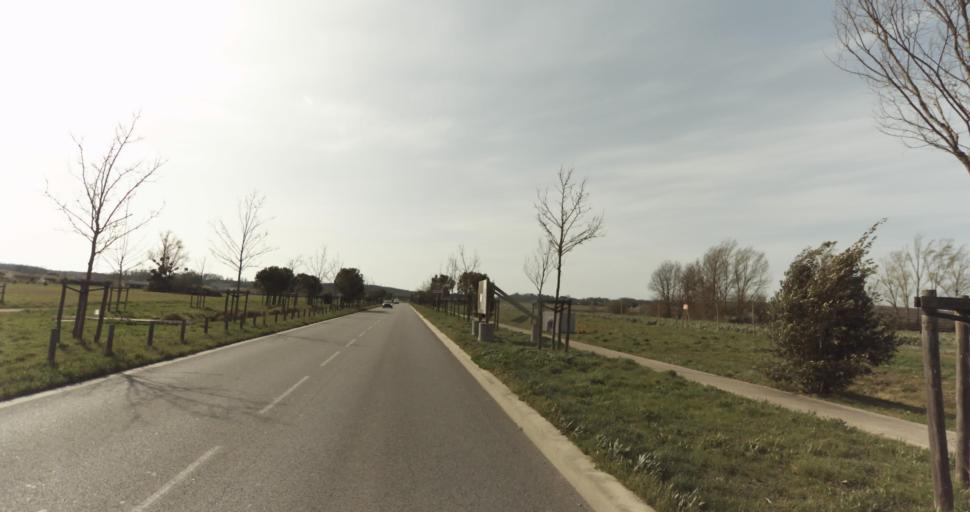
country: FR
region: Midi-Pyrenees
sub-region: Departement du Tarn
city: Saint-Sulpice-la-Pointe
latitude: 43.7602
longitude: 1.6581
